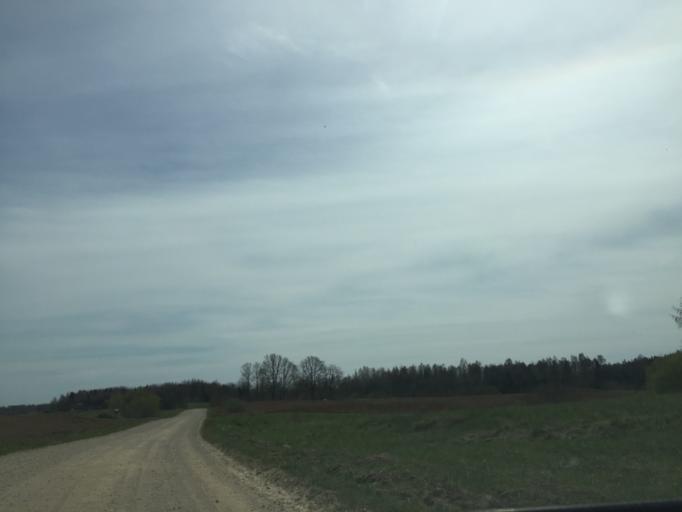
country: LV
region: Ludzas Rajons
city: Ludza
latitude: 56.5822
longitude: 27.5439
